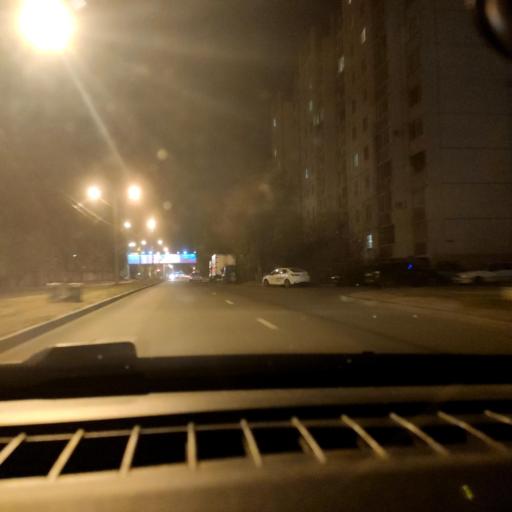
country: RU
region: Voronezj
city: Voronezh
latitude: 51.7057
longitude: 39.1956
